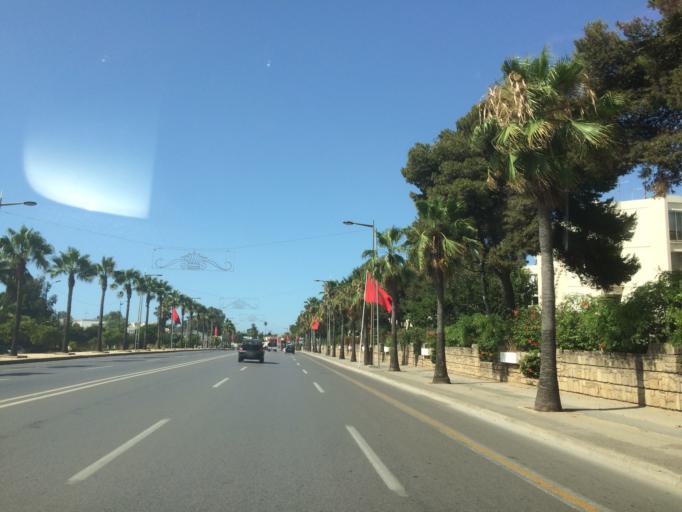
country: MA
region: Rabat-Sale-Zemmour-Zaer
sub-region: Rabat
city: Rabat
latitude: 33.9908
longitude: -6.8276
